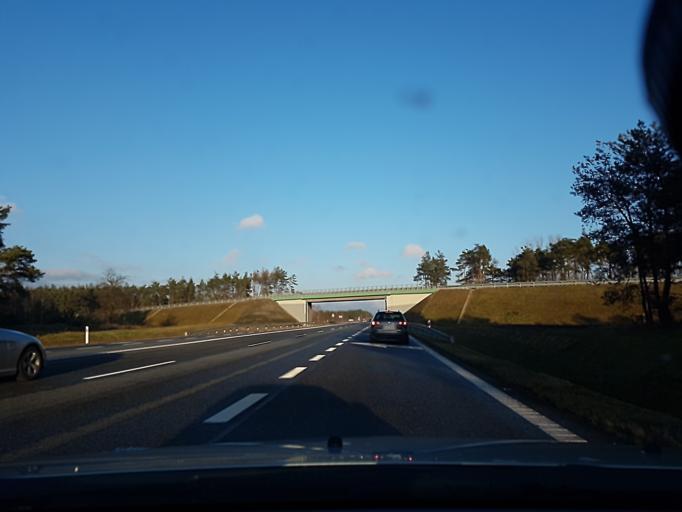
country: PL
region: Masovian Voivodeship
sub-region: Powiat gostyninski
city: Gostynin
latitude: 52.4371
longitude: 19.5069
